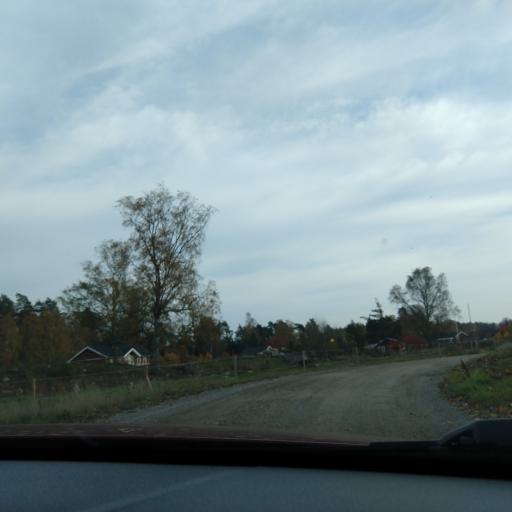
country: SE
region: Stockholm
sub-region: Vallentuna Kommun
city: Vallentuna
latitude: 59.5279
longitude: 18.0125
